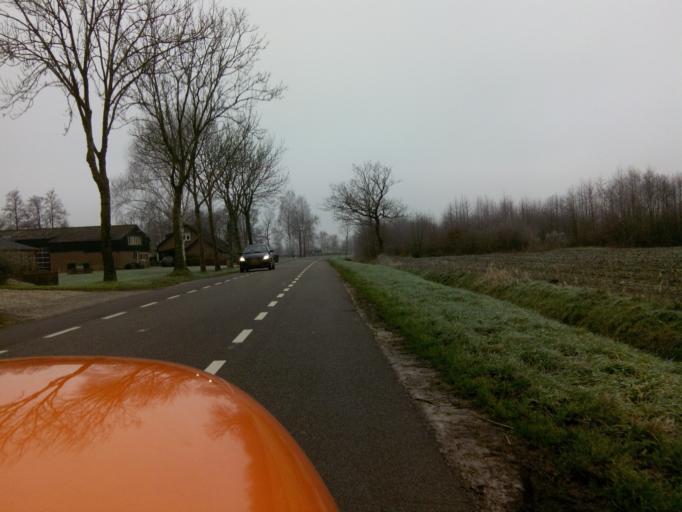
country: NL
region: Gelderland
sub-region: Gemeente Barneveld
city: Zwartebroek
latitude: 52.1800
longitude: 5.5146
